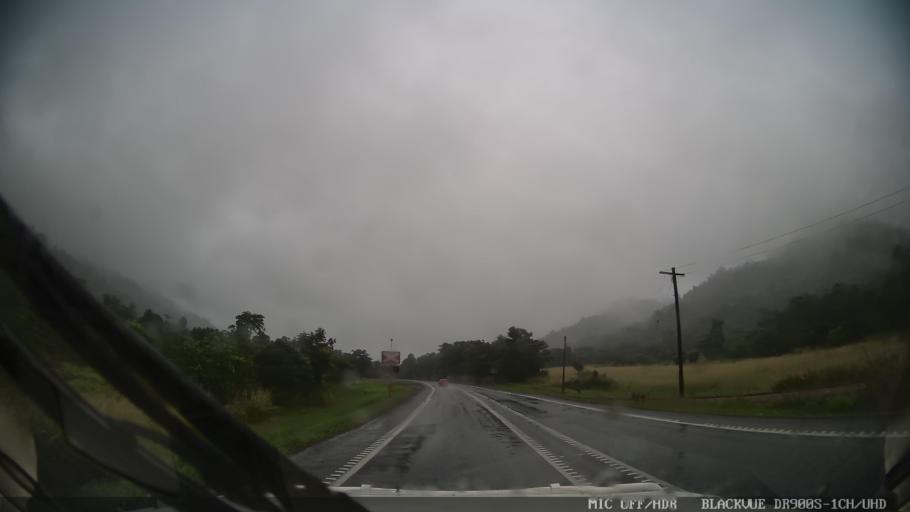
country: AU
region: Queensland
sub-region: Cassowary Coast
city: Innisfail
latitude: -17.8601
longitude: 145.9864
